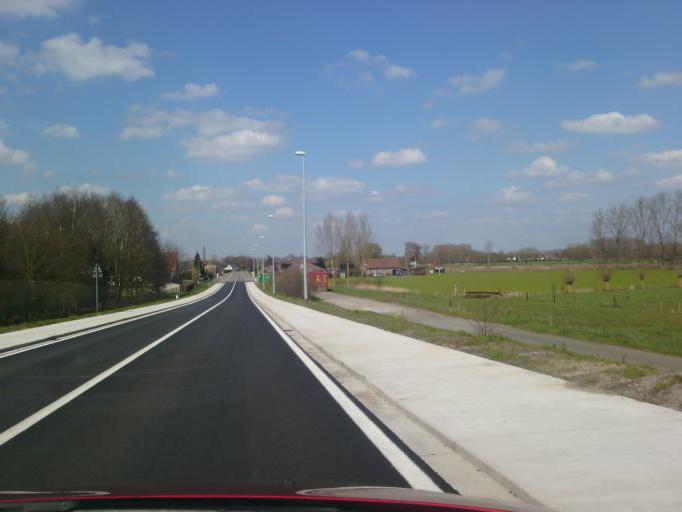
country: BE
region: Flanders
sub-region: Provincie Oost-Vlaanderen
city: Lokeren
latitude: 51.0741
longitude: 3.9472
